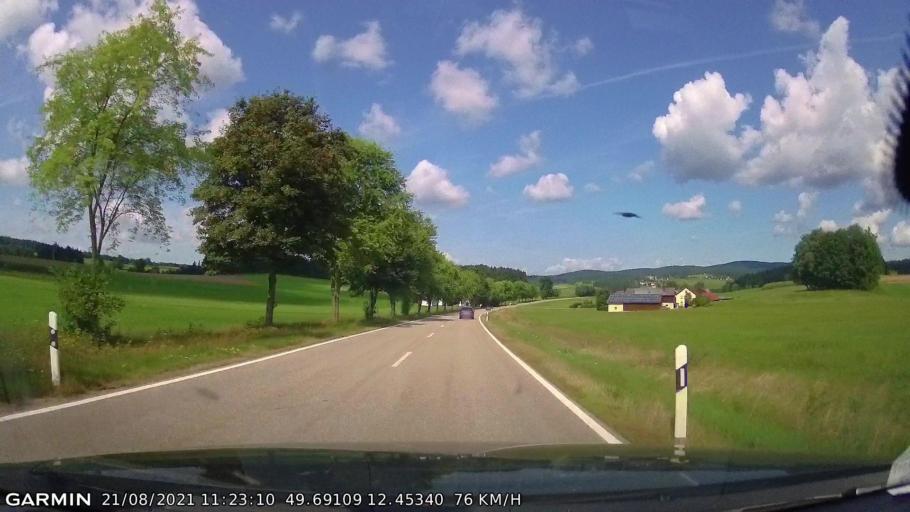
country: DE
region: Bavaria
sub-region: Upper Palatinate
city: Georgenberg
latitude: 49.6911
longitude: 12.4534
